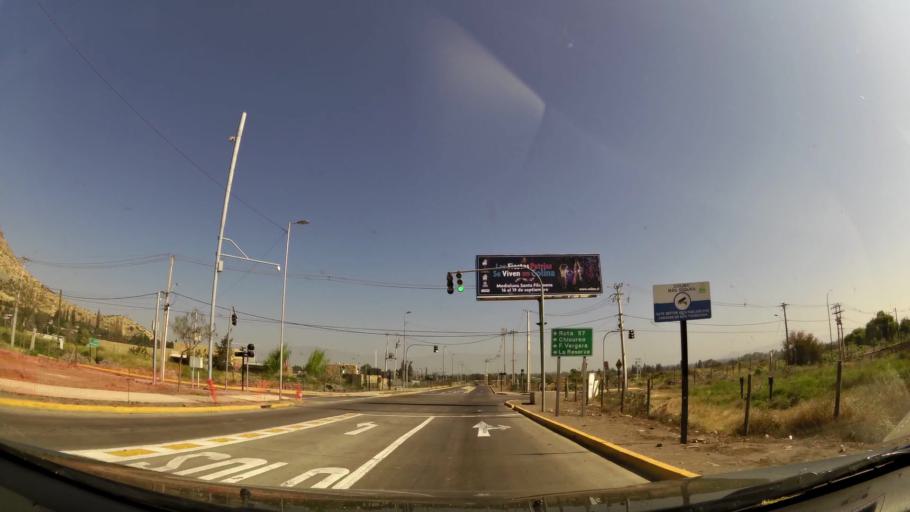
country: CL
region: Santiago Metropolitan
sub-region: Provincia de Chacabuco
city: Chicureo Abajo
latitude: -33.3031
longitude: -70.6824
